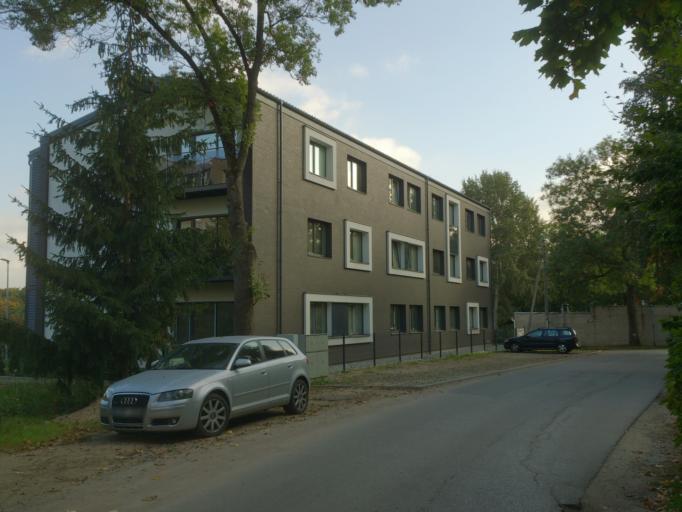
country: LT
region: Kauno apskritis
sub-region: Kaunas
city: Aleksotas
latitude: 54.8754
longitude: 23.9195
